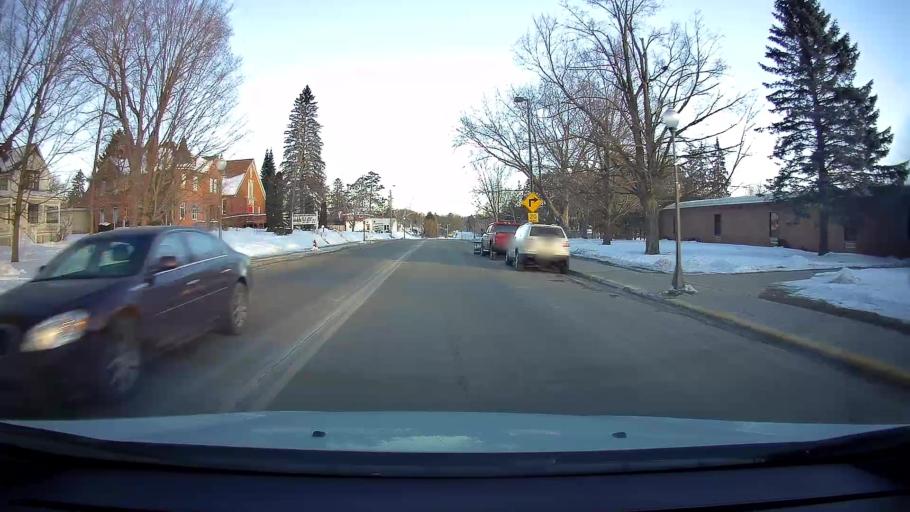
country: US
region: Wisconsin
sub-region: Barron County
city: Cumberland
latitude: 45.5382
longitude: -92.0218
